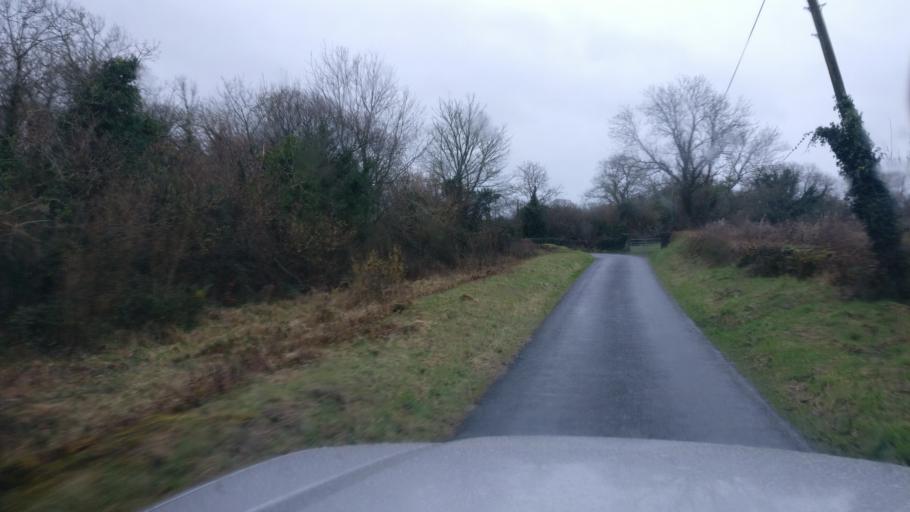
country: IE
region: Connaught
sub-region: County Galway
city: Ballinasloe
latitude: 53.2945
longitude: -8.2739
